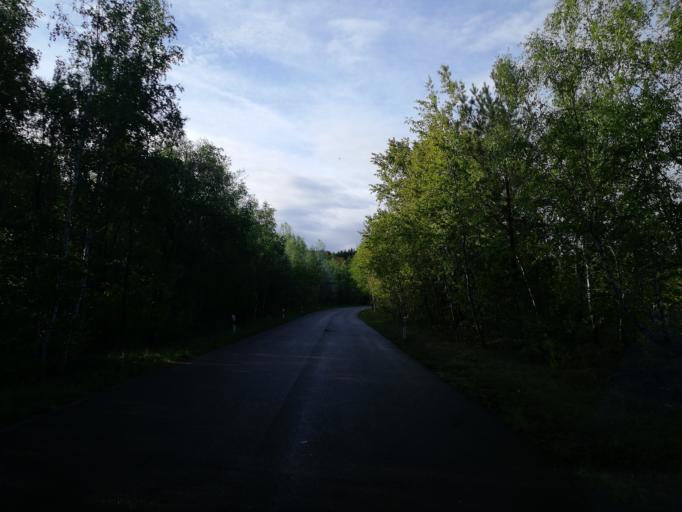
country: DE
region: Brandenburg
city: Lauchhammer
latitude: 51.5258
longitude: 13.7718
